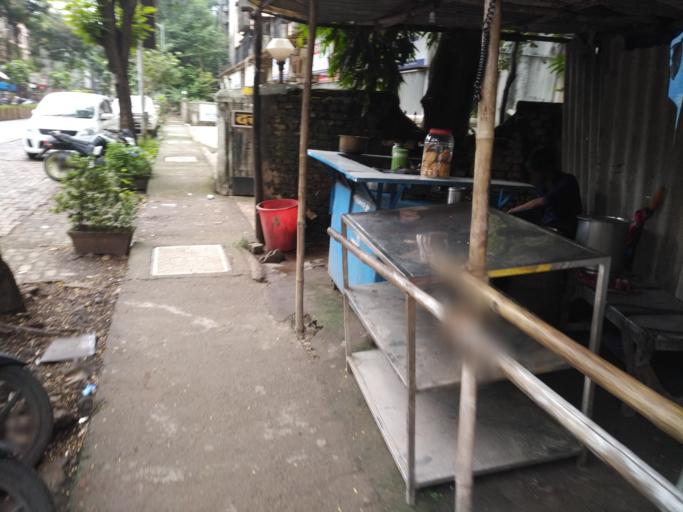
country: IN
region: Maharashtra
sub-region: Mumbai Suburban
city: Borivli
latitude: 19.2429
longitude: 72.8652
